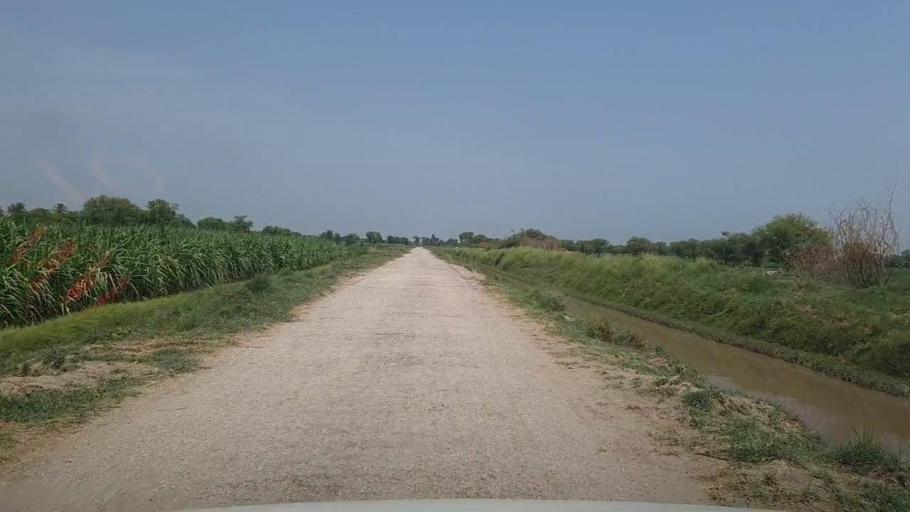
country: PK
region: Sindh
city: Karaundi
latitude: 26.8836
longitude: 68.3345
